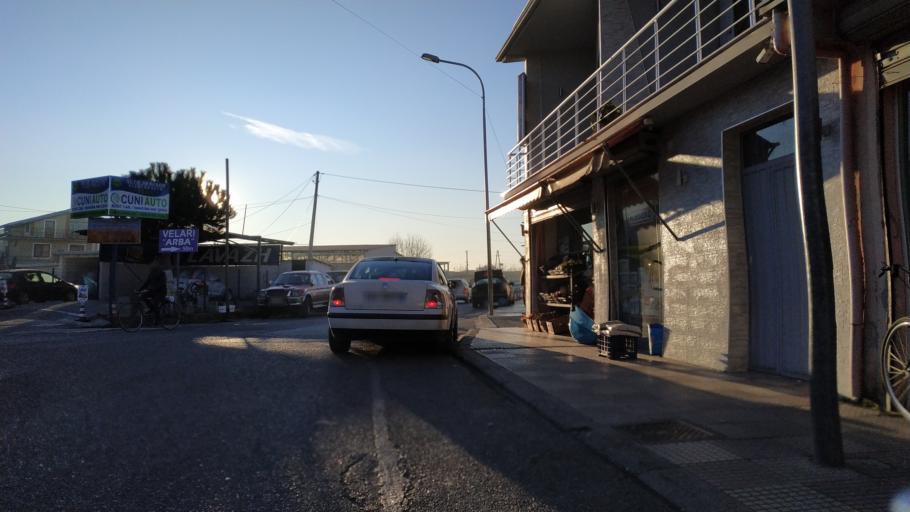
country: AL
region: Shkoder
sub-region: Rrethi i Shkodres
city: Shkoder
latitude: 42.0616
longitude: 19.5209
